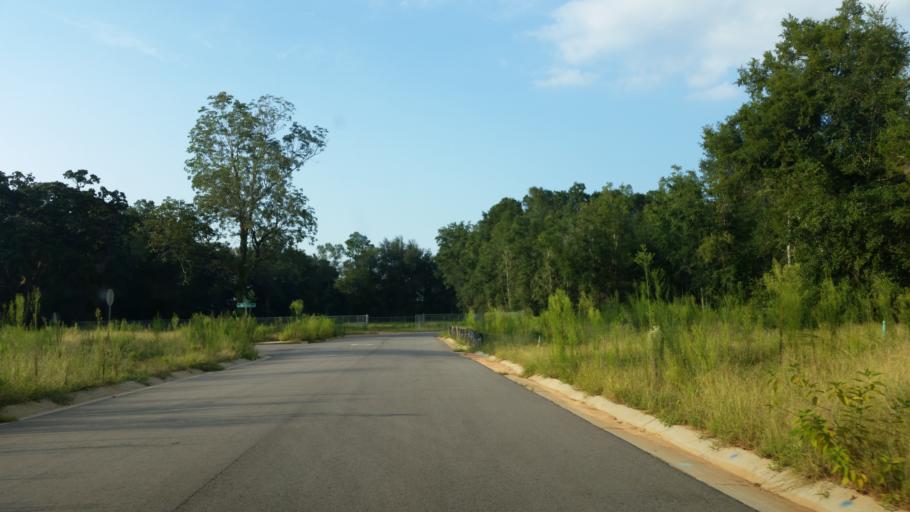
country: US
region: Florida
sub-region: Santa Rosa County
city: Pace
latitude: 30.6152
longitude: -87.1331
